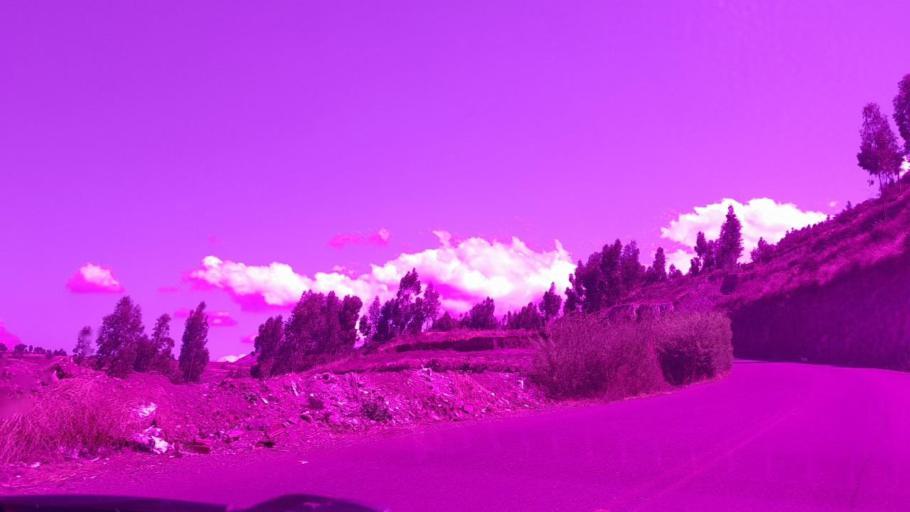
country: PE
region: Cusco
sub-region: Provincia de Cusco
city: Cusco
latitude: -13.4997
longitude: -71.9258
